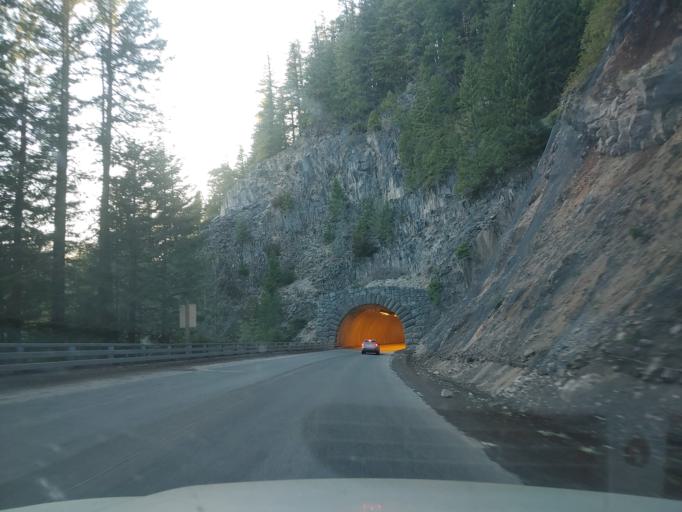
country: US
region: Oregon
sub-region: Lane County
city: Oakridge
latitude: 43.6140
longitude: -122.1325
